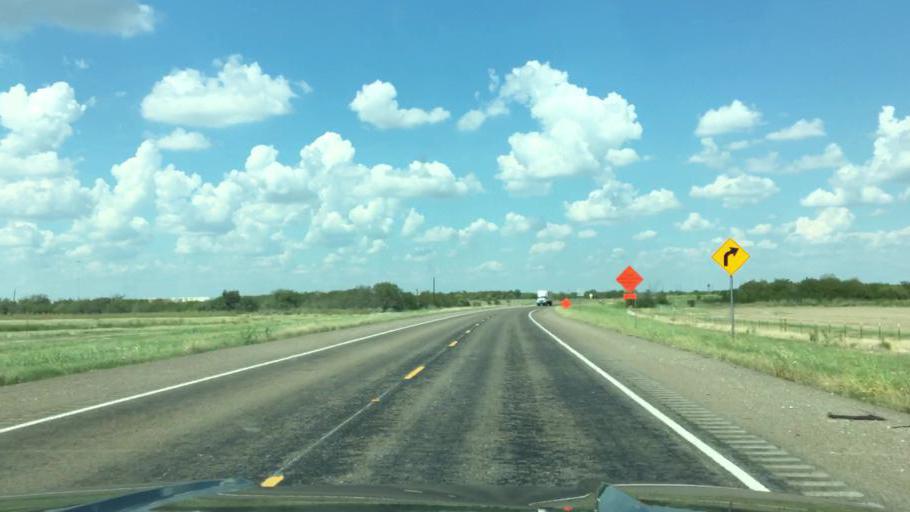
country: US
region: Texas
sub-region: Tarrant County
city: Haslet
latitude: 33.0026
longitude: -97.3423
